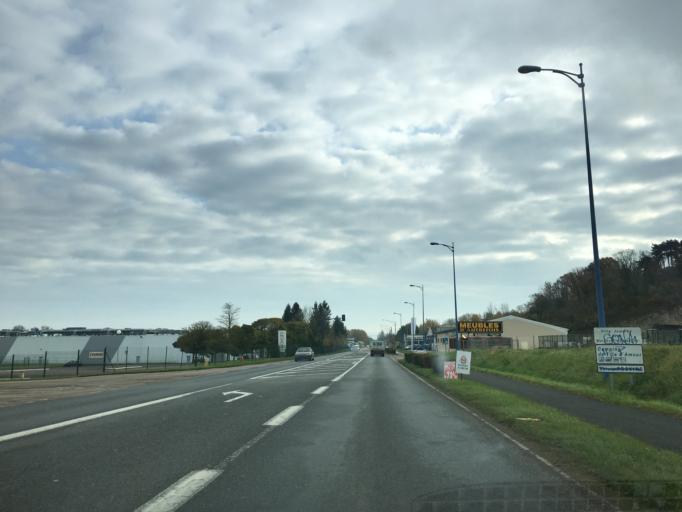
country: FR
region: Bourgogne
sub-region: Departement de l'Yonne
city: Pont-sur-Yonne
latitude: 48.2944
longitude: 3.1942
